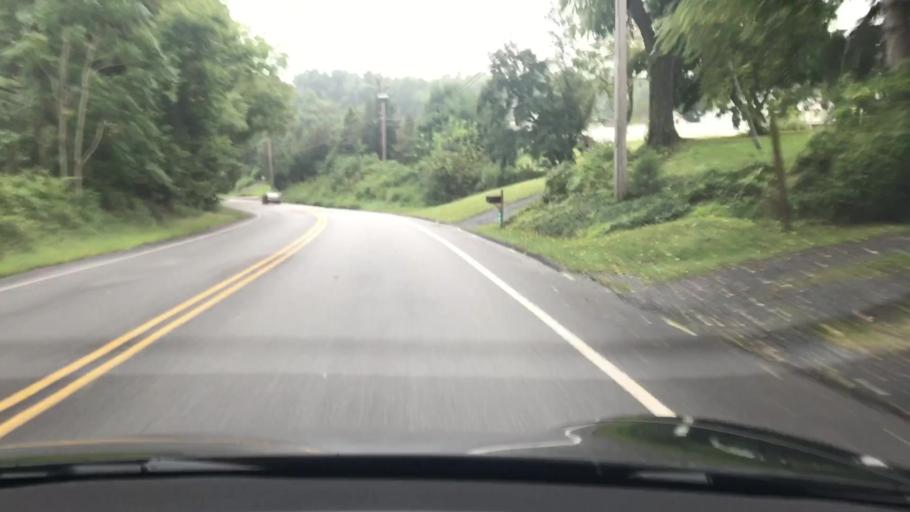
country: US
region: Pennsylvania
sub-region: York County
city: Valley Green
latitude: 40.1659
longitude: -76.8220
